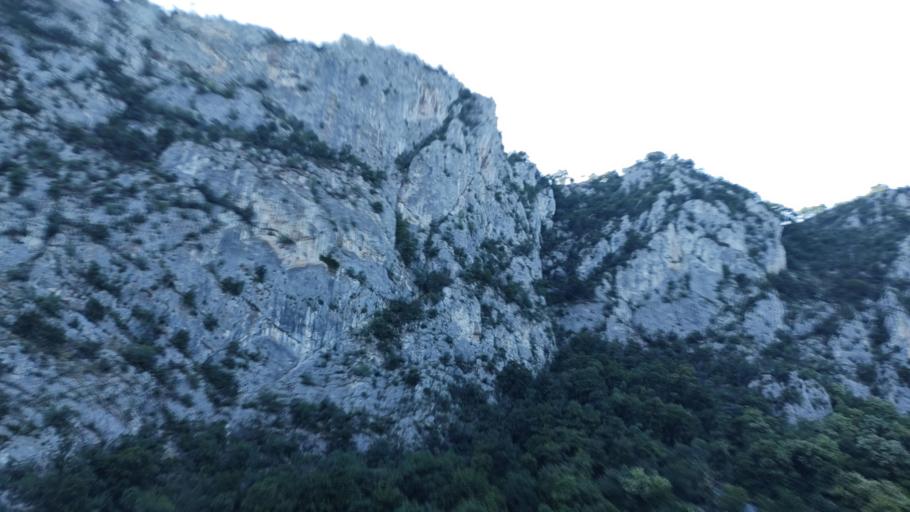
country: RO
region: Mehedinti
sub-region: Comuna Dubova
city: Dubova
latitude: 44.6016
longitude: 22.2660
